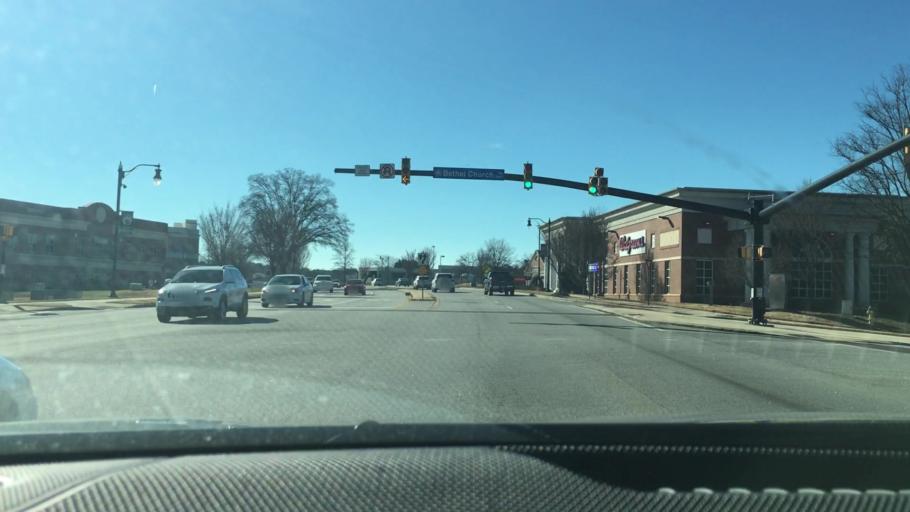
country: US
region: North Carolina
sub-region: Mecklenburg County
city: Cornelius
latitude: 35.4804
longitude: -80.8882
